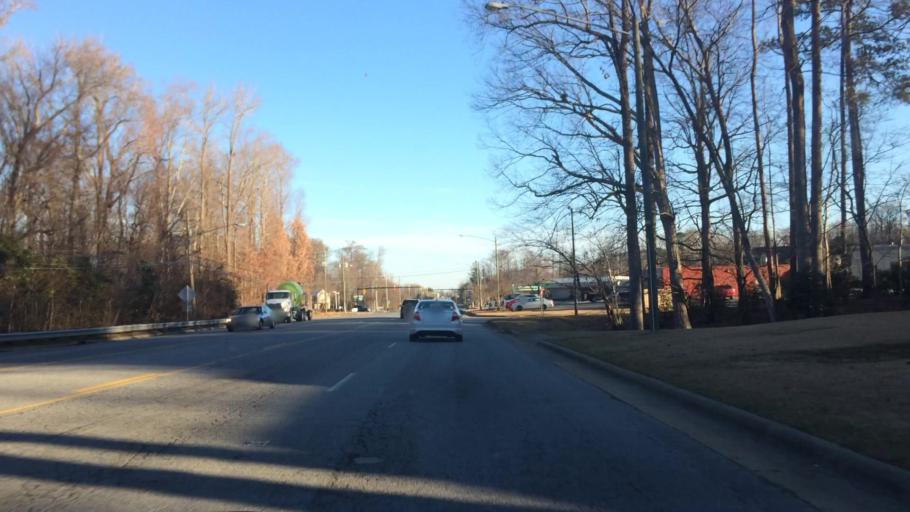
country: US
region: North Carolina
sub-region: Pitt County
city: Greenville
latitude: 35.5888
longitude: -77.3787
